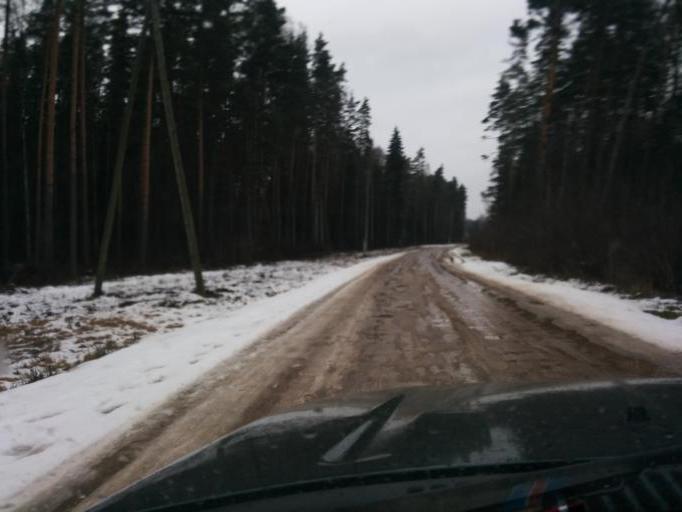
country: LV
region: Ozolnieku
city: Ozolnieki
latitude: 56.6812
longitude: 23.7608
